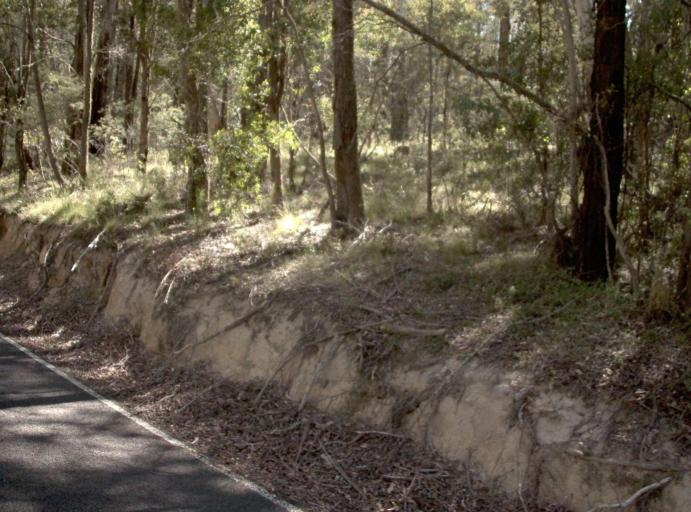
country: AU
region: New South Wales
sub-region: Bombala
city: Bombala
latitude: -37.1556
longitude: 148.7247
